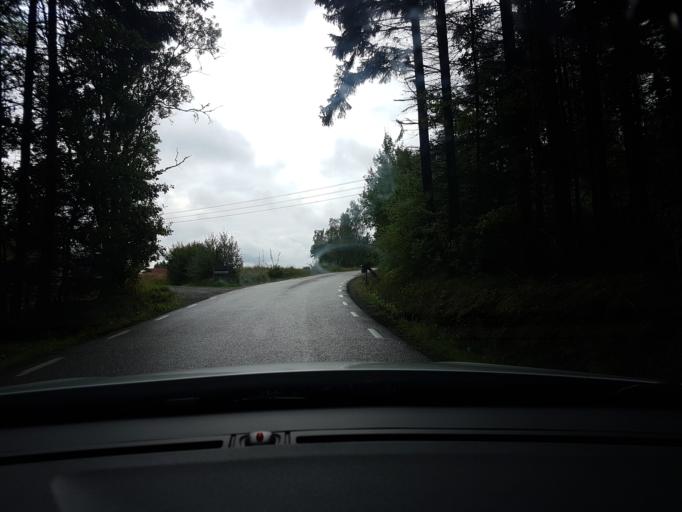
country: SE
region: Vaestra Goetaland
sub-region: Ale Kommun
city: Alvangen
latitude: 57.9229
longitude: 12.1342
